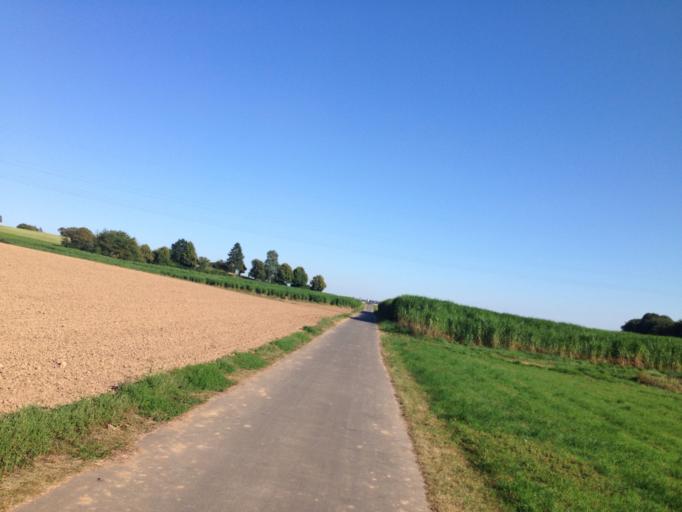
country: DE
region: Hesse
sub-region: Regierungsbezirk Giessen
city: Grunberg
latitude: 50.6126
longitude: 8.9557
